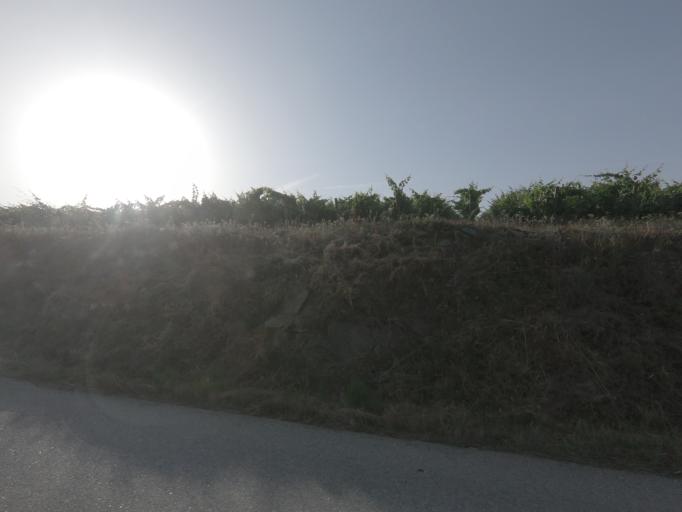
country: PT
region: Vila Real
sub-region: Sabrosa
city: Sabrosa
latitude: 41.2481
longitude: -7.4661
